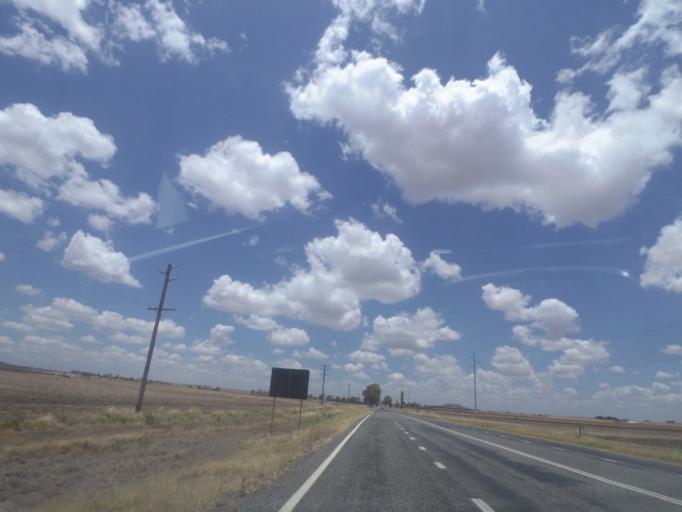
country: AU
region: Queensland
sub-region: Toowoomba
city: Top Camp
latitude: -27.9214
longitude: 151.9830
